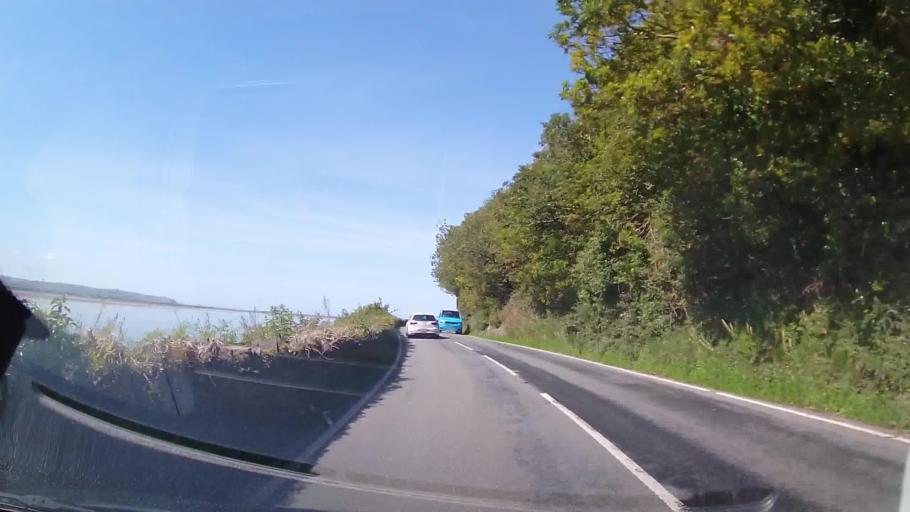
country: GB
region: Wales
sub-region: Gwynedd
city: Tywyn
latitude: 52.5523
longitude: -3.9987
